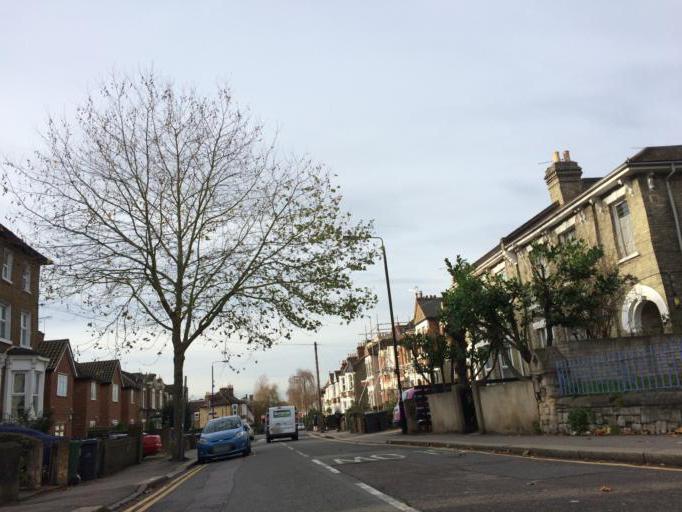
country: GB
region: England
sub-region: Greater London
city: Walthamstow
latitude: 51.5818
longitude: -0.0150
